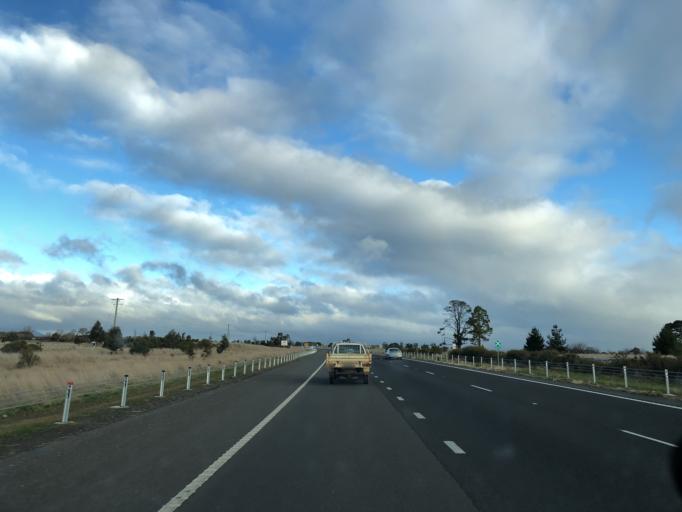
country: AU
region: Victoria
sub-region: Mount Alexander
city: Castlemaine
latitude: -37.1956
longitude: 144.4053
